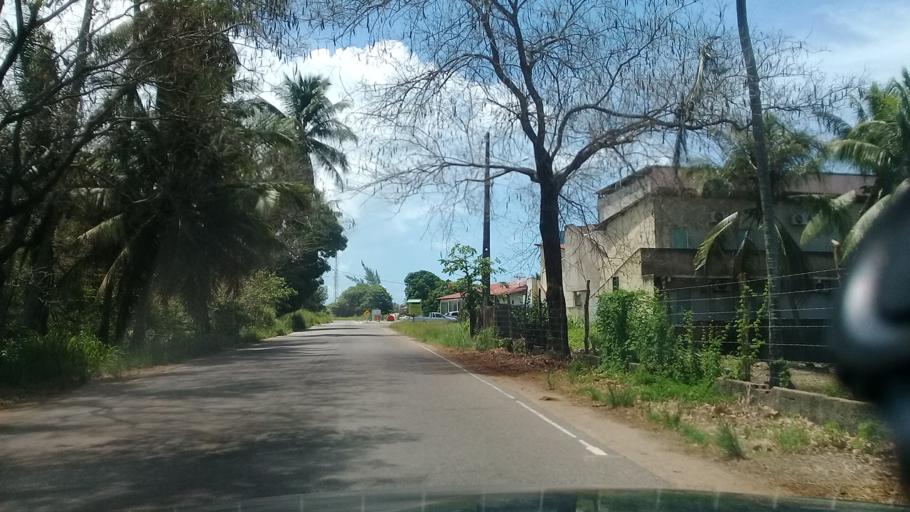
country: BR
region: Pernambuco
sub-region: Sirinhaem
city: Sirinhaem
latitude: -8.6230
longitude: -35.0618
